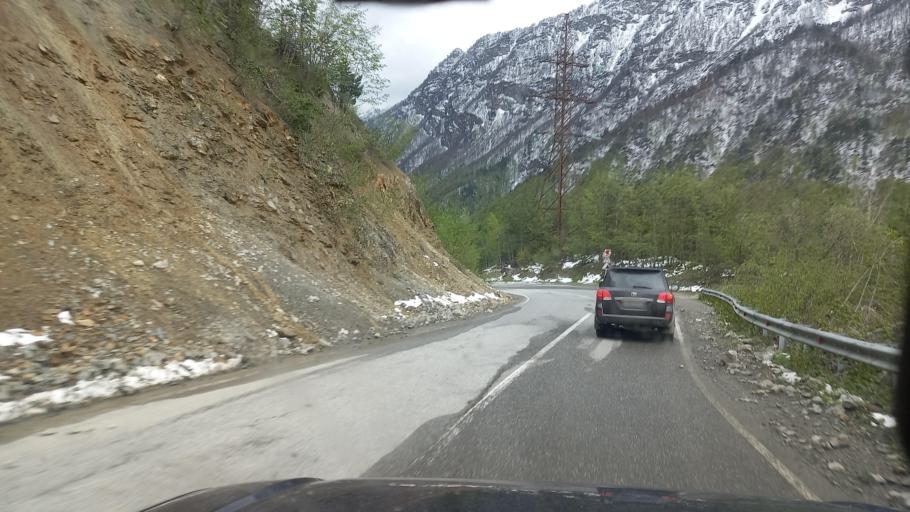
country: RU
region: North Ossetia
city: Mizur
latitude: 42.8030
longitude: 43.9513
